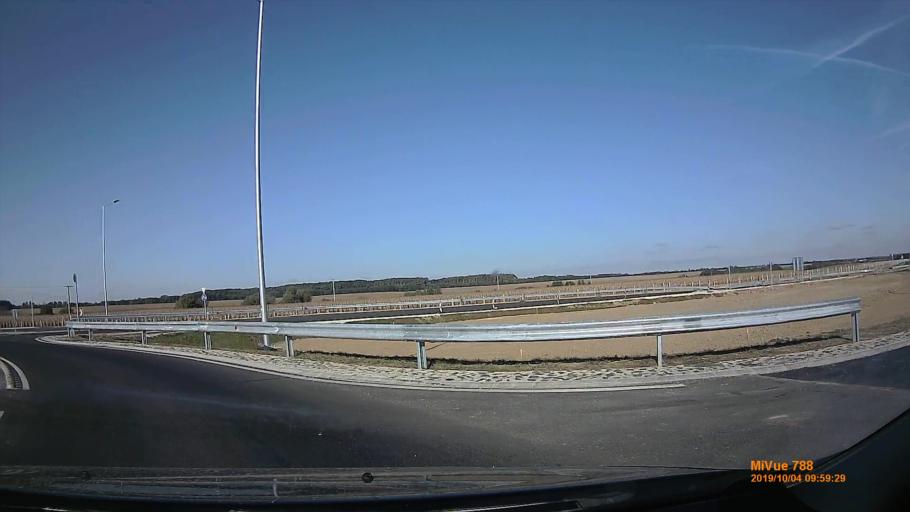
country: HU
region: Somogy
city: Kaposvar
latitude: 46.4251
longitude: 17.7735
